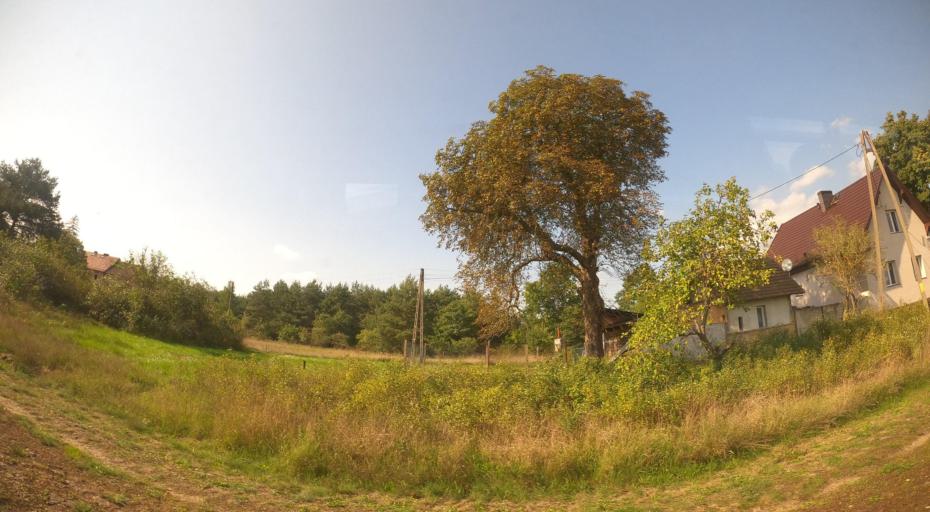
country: PL
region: Lubusz
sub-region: Powiat zielonogorski
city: Nowogrod Bobrzanski
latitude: 51.8436
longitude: 15.2673
